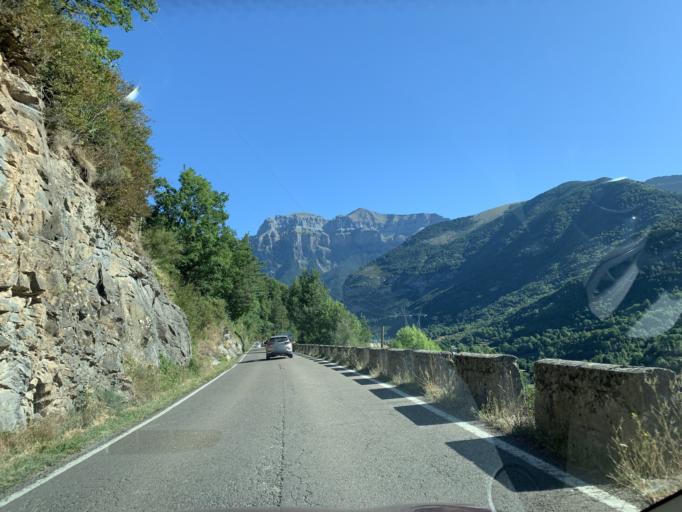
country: ES
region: Aragon
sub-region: Provincia de Huesca
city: Broto
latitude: 42.6183
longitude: -0.1162
